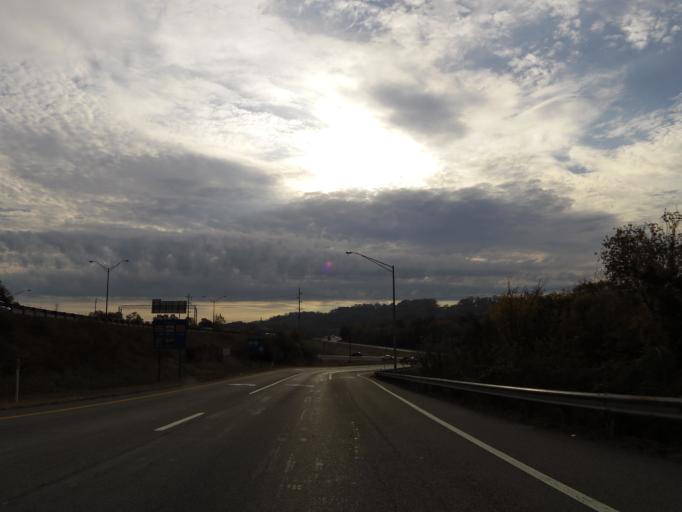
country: US
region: Tennessee
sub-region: Knox County
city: Knoxville
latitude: 36.0111
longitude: -83.8439
